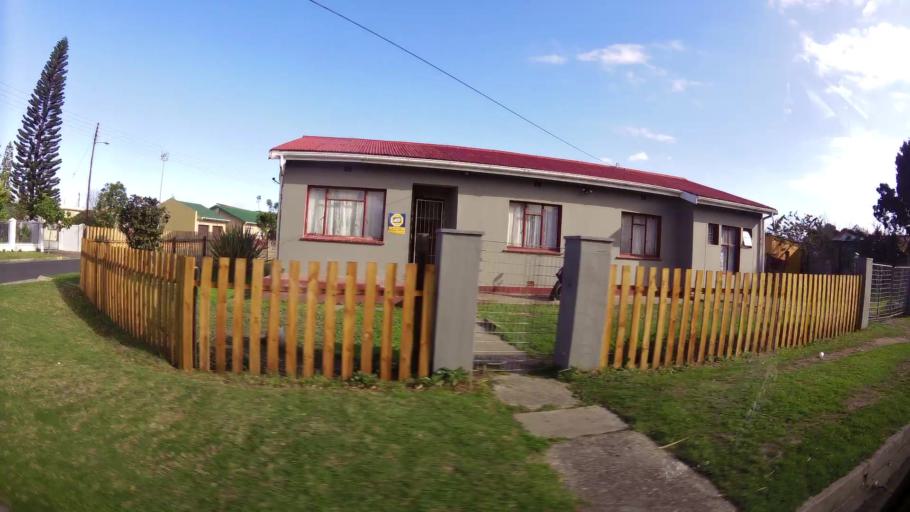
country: ZA
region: Western Cape
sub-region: Eden District Municipality
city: George
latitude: -33.9676
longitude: 22.4800
